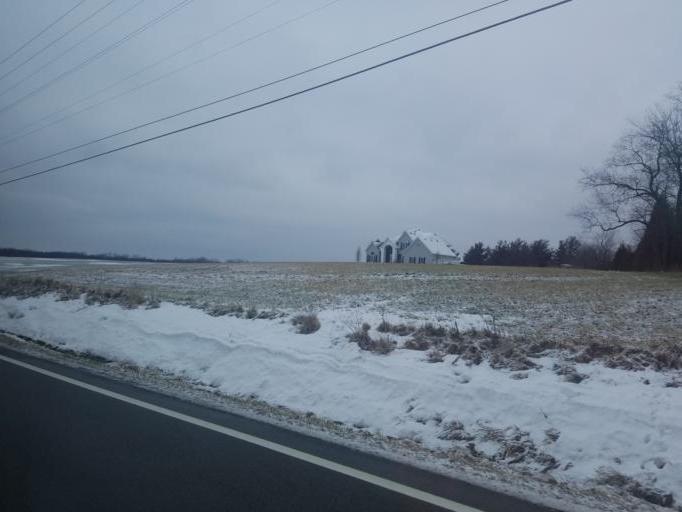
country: US
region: Ohio
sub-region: Licking County
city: Johnstown
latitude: 40.1675
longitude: -82.7038
